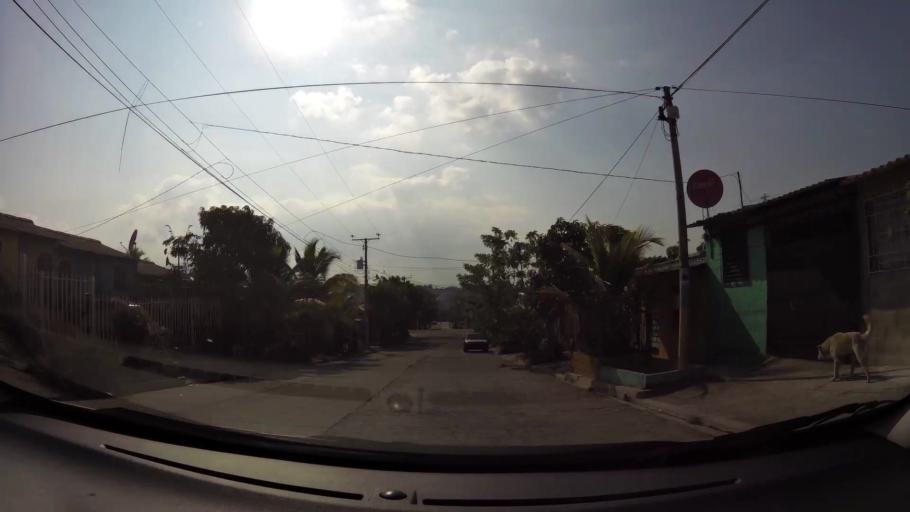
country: SV
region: San Salvador
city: Ilopango
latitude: 13.7293
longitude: -89.1113
